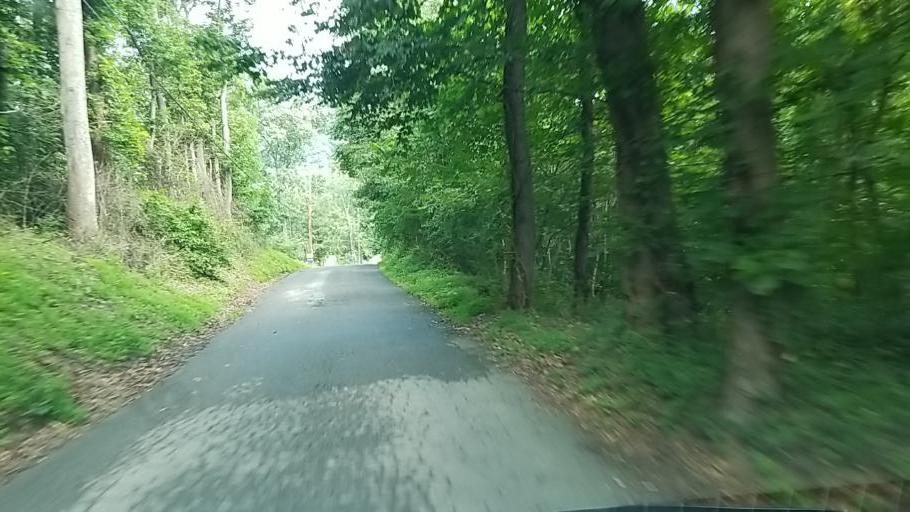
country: US
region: Pennsylvania
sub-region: Dauphin County
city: Millersburg
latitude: 40.5204
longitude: -76.9383
